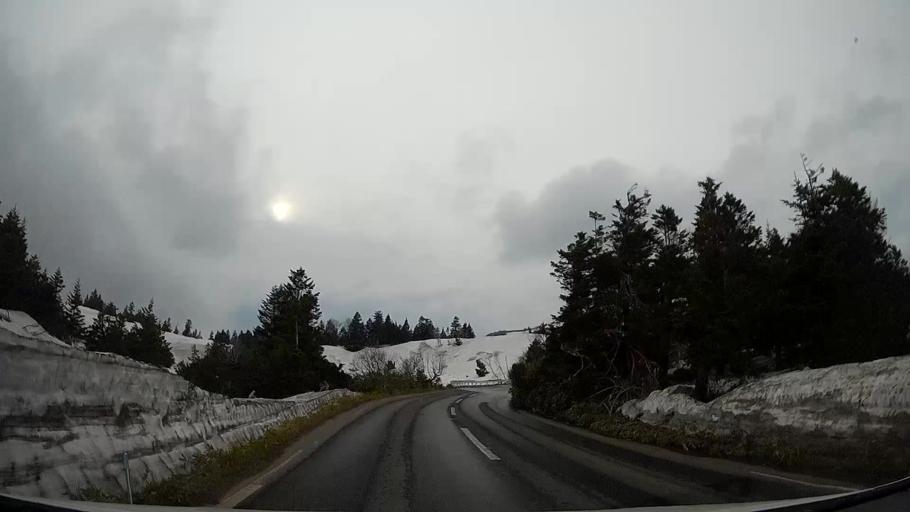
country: JP
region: Aomori
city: Aomori Shi
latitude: 40.6325
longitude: 140.8872
